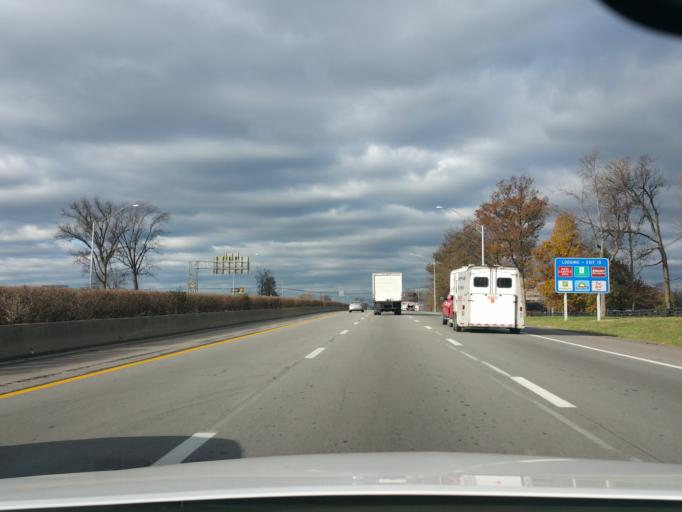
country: US
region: Kentucky
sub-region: Jefferson County
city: Douglass Hills
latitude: 38.2230
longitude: -85.5641
